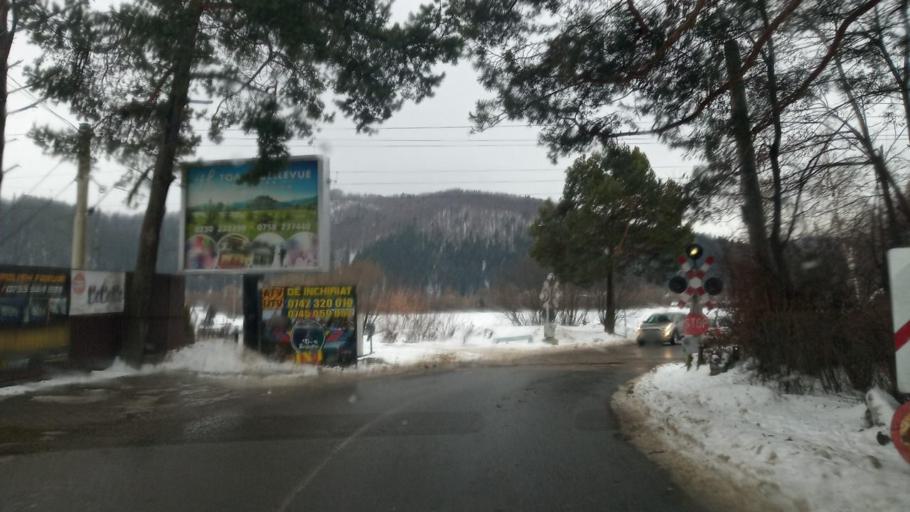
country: RO
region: Suceava
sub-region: Oras Gura Humorului
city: Gura Humorului
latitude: 47.5478
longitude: 25.8727
